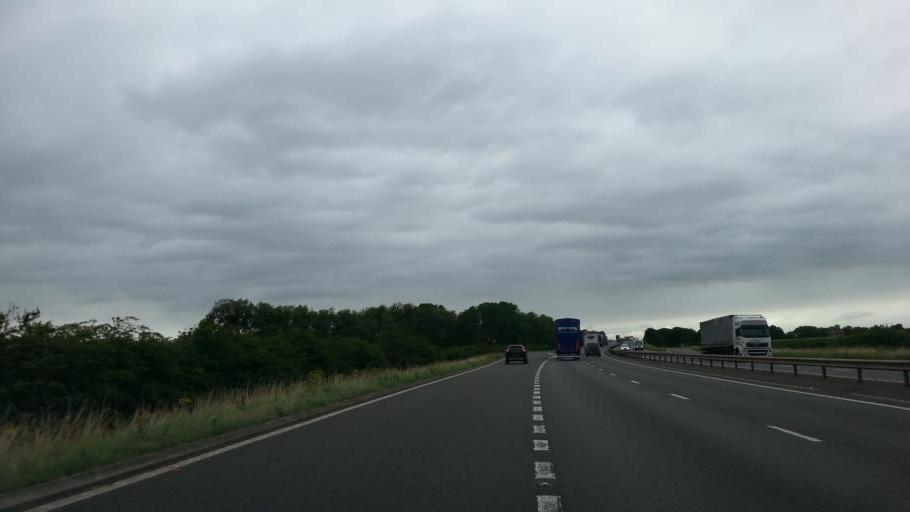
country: GB
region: England
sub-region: Nottinghamshire
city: Newark on Trent
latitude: 53.1153
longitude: -0.8161
